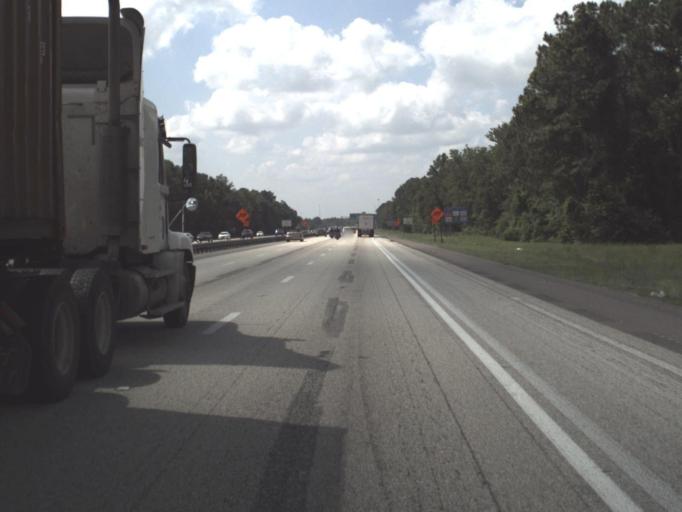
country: US
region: Florida
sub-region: Saint Johns County
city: Fruit Cove
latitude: 30.1299
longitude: -81.5291
